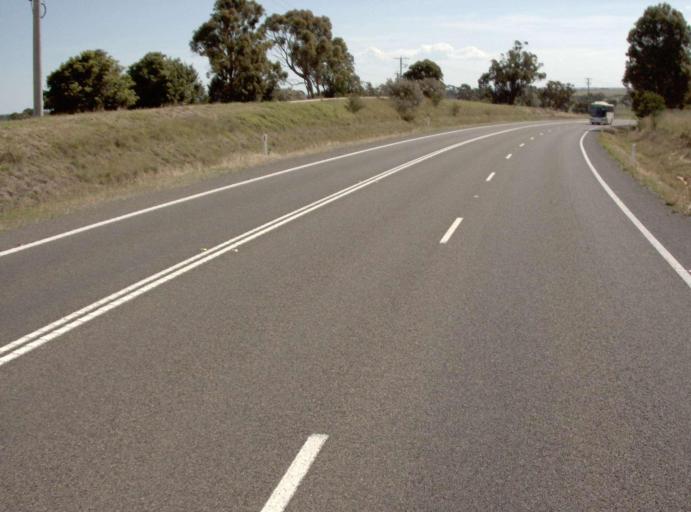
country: AU
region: Victoria
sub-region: East Gippsland
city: Lakes Entrance
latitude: -37.8216
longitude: 147.8074
